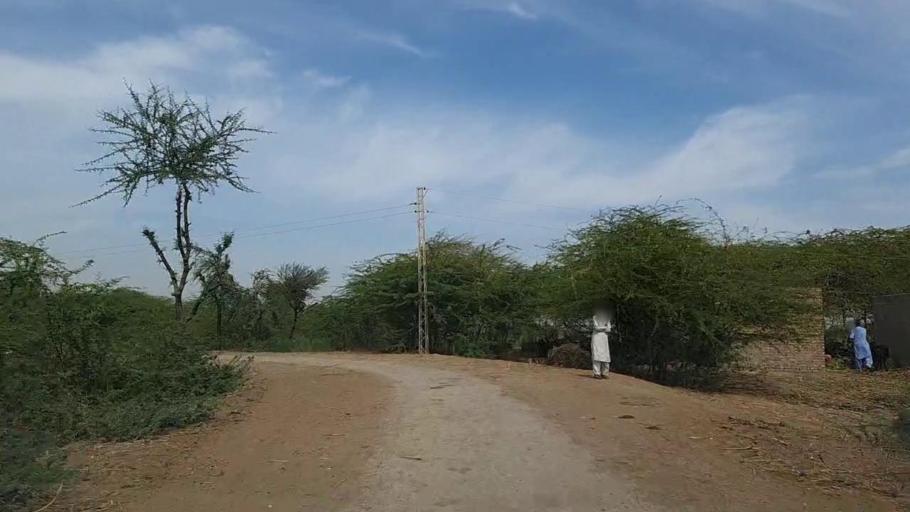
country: PK
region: Sindh
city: Samaro
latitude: 25.3000
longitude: 69.4239
